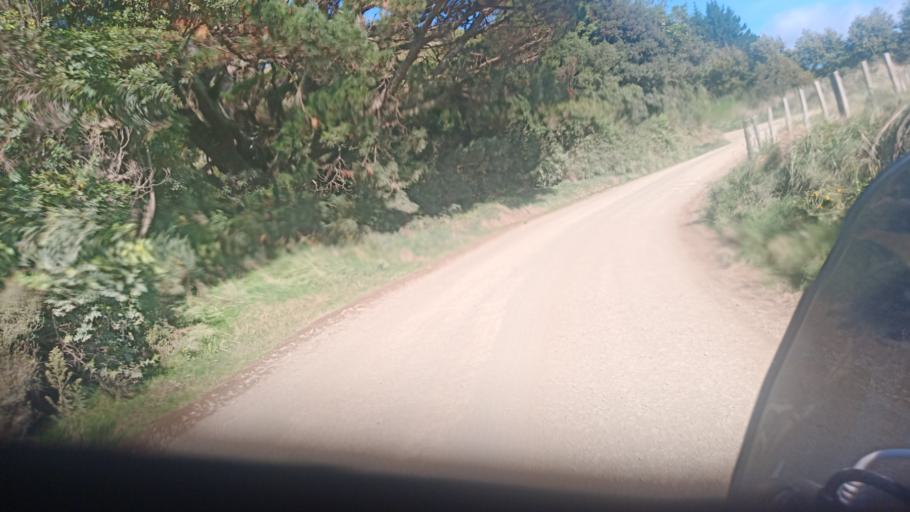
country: NZ
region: Gisborne
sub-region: Gisborne District
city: Gisborne
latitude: -38.4325
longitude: 177.5557
